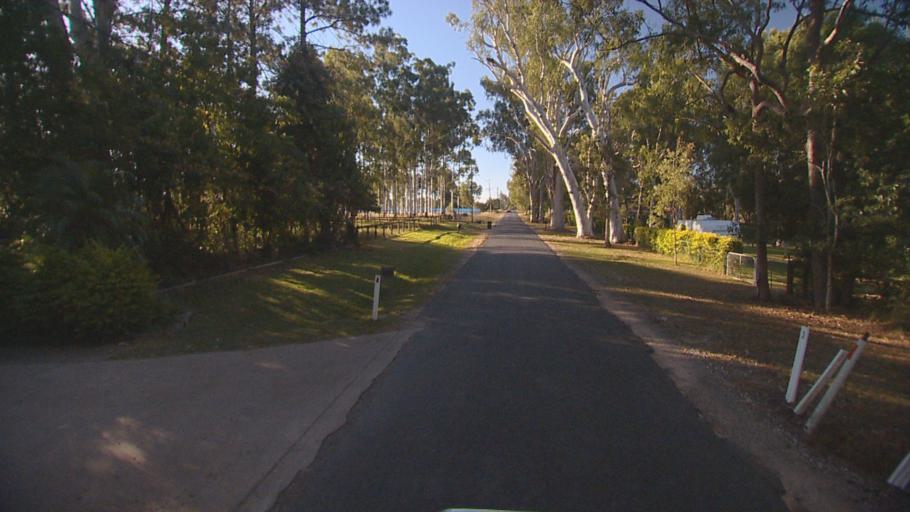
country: AU
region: Queensland
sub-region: Logan
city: Chambers Flat
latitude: -27.7810
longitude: 153.0873
